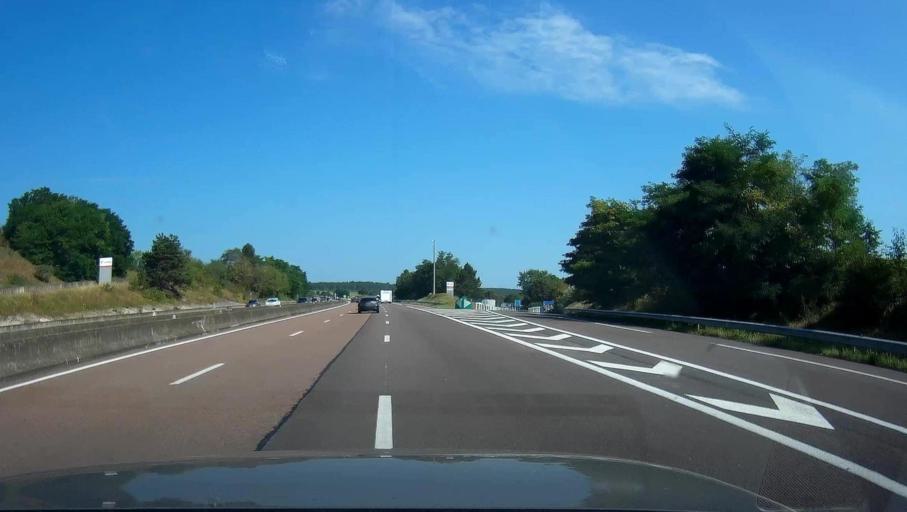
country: FR
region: Bourgogne
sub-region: Departement de la Cote-d'Or
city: Selongey
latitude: 47.5840
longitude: 5.2105
